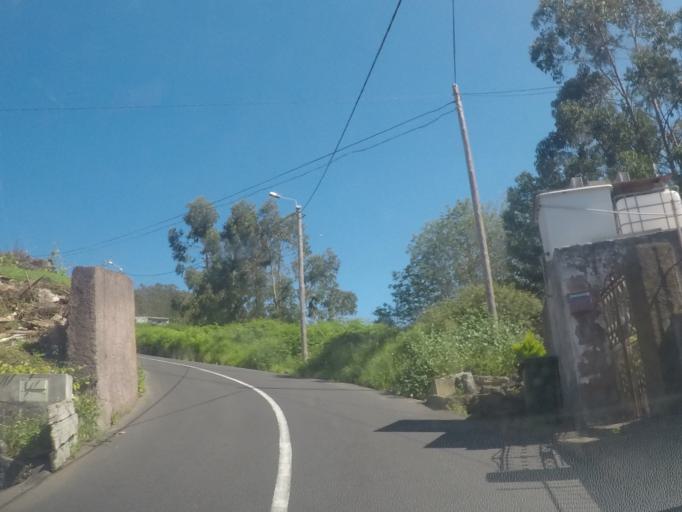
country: PT
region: Madeira
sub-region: Camara de Lobos
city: Curral das Freiras
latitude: 32.6810
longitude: -16.9673
